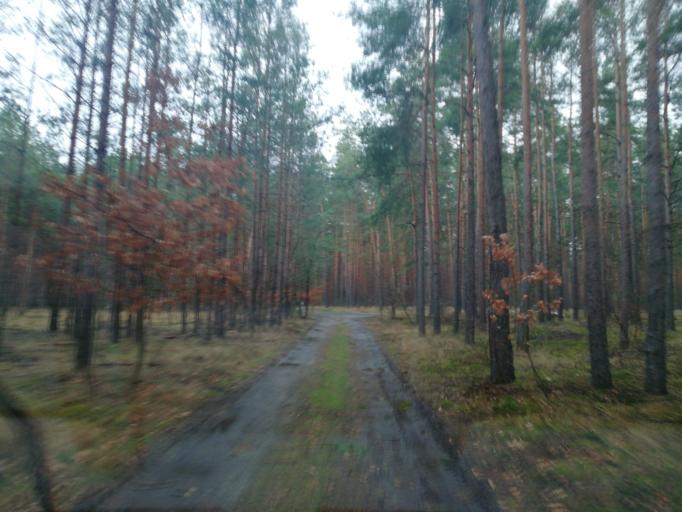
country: DE
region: Brandenburg
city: Schonborn
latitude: 51.6647
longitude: 13.4892
